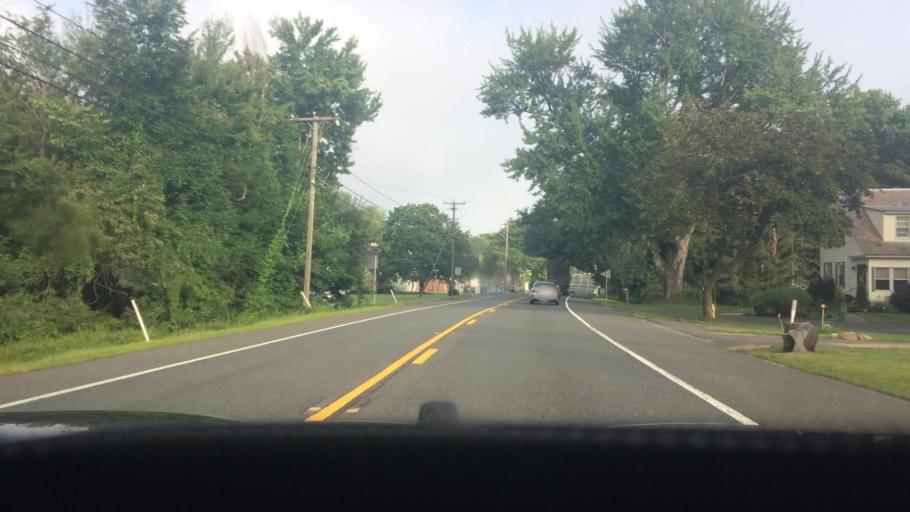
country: US
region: Massachusetts
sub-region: Franklin County
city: Turners Falls
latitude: 42.6099
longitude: -72.5421
